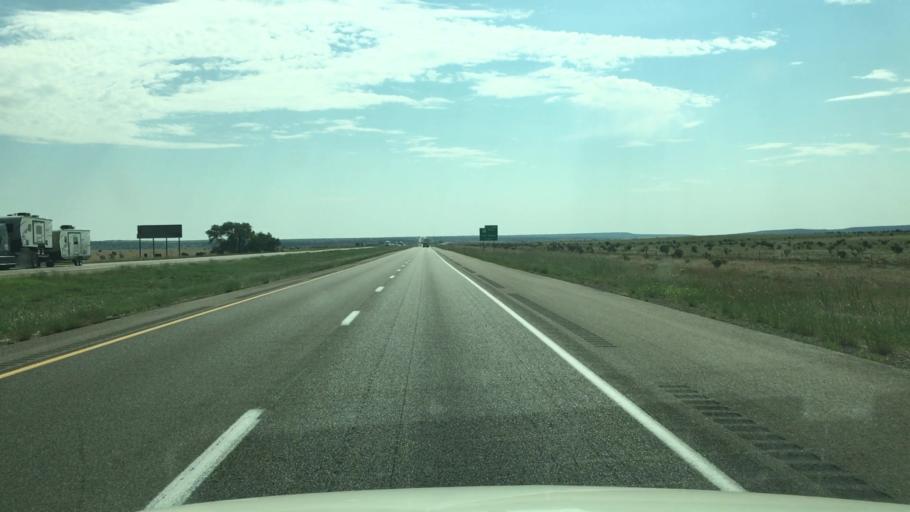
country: US
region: New Mexico
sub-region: Guadalupe County
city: Santa Rosa
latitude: 34.9775
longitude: -105.0143
